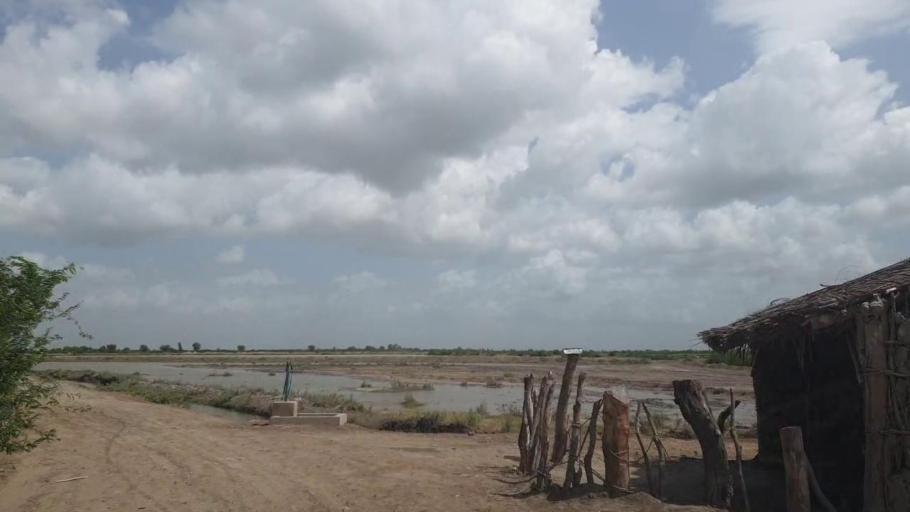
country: PK
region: Sindh
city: Tando Bago
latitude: 24.6493
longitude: 68.9980
